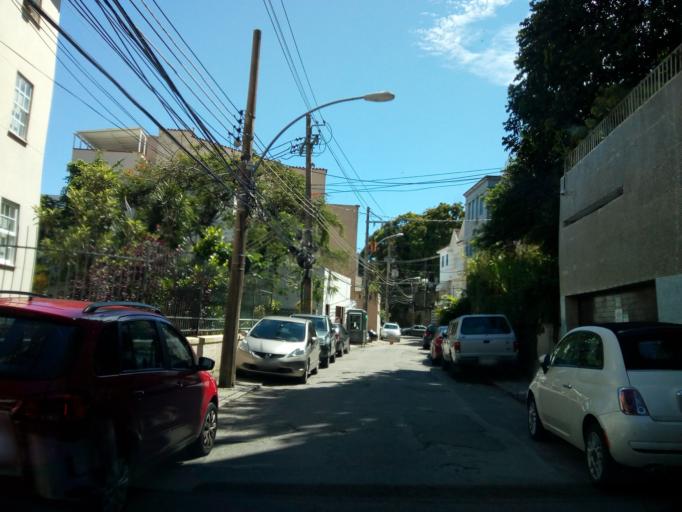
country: BR
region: Rio de Janeiro
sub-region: Rio De Janeiro
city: Rio de Janeiro
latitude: -22.9469
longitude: -43.1614
